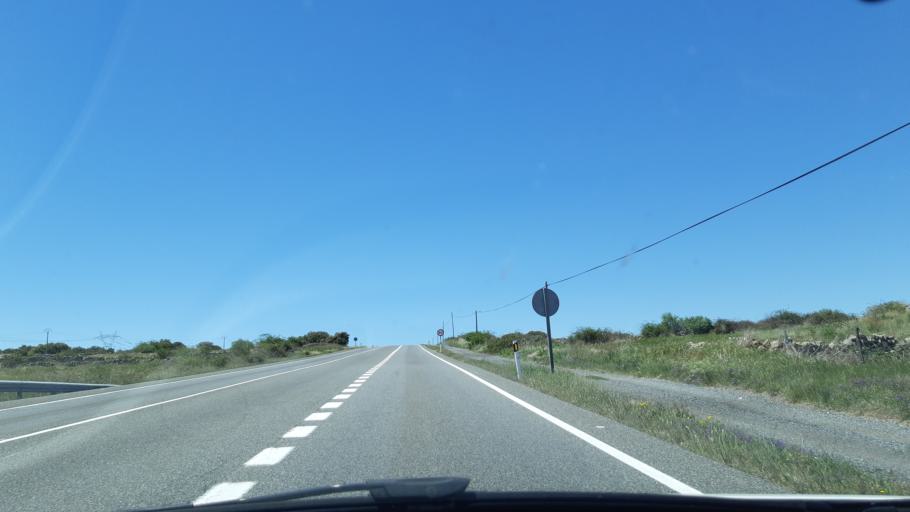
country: ES
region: Castille and Leon
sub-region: Provincia de Segovia
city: Zarzuela del Monte
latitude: 40.7593
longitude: -4.3354
